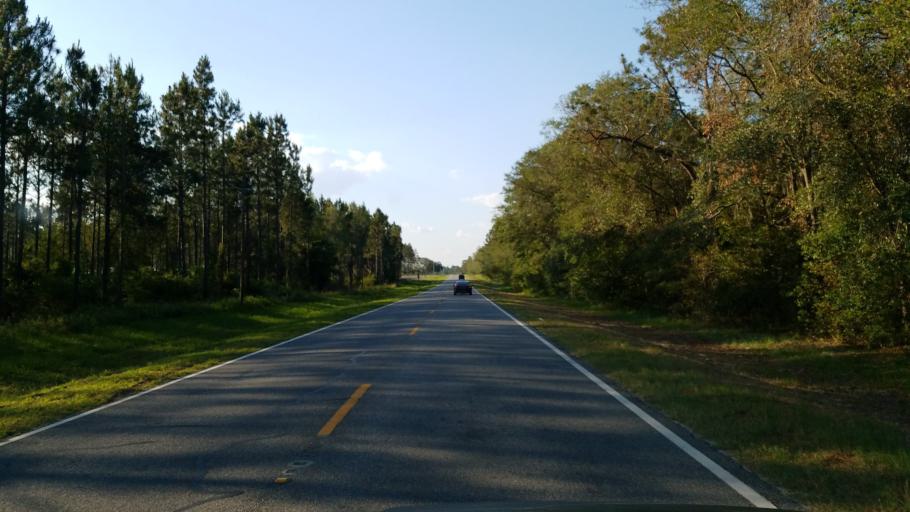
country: US
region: Georgia
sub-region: Lanier County
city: Lakeland
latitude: 31.0171
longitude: -83.0650
